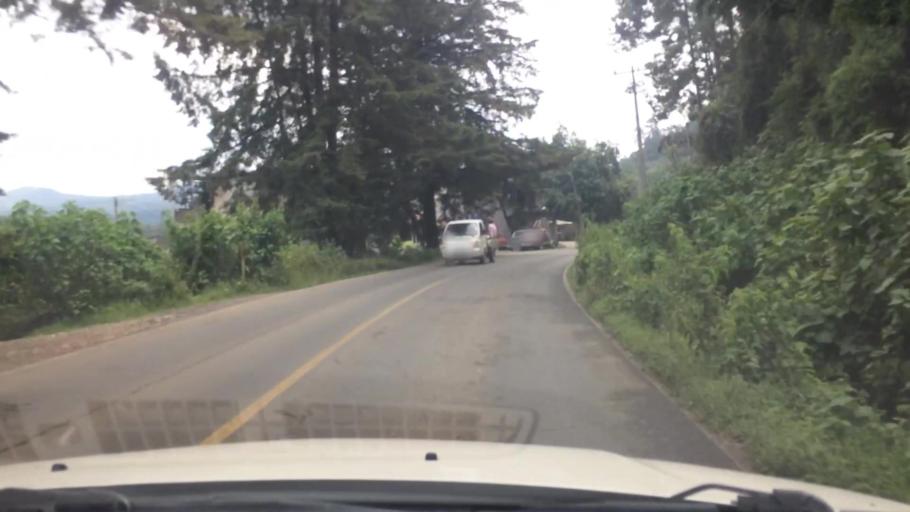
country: MX
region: Mexico
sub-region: Valle de Bravo
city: Cuadrilla de Dolores
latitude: 19.1492
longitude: -100.0583
